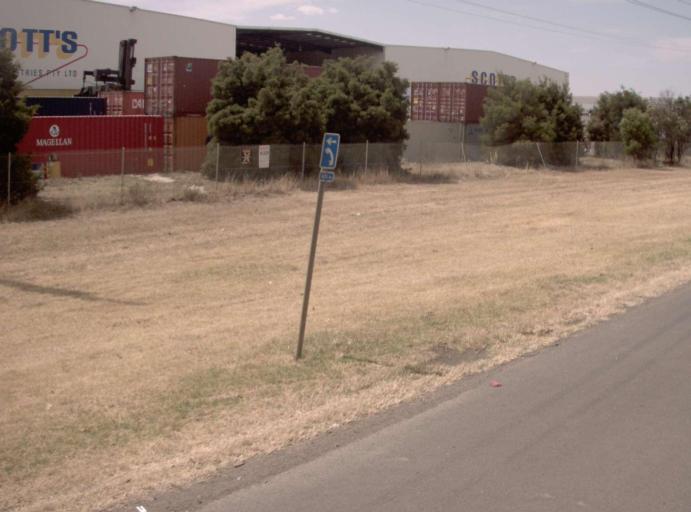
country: AU
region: Victoria
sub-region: Hobsons Bay
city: Laverton
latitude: -37.8402
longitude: 144.7940
